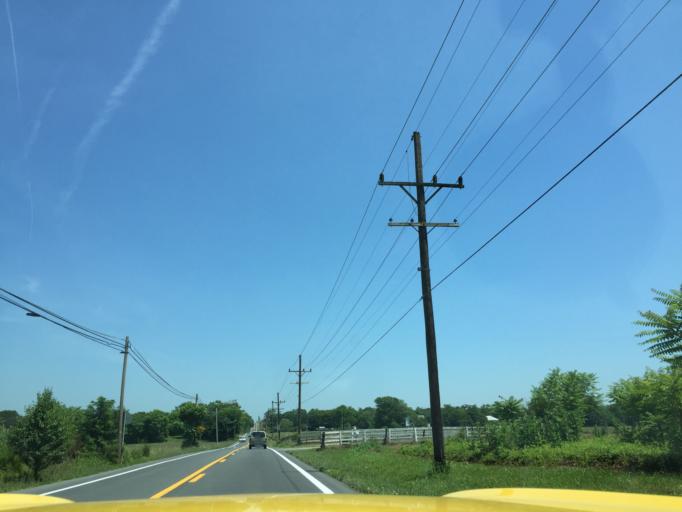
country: US
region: West Virginia
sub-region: Jefferson County
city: Ranson
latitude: 39.3034
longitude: -77.9435
